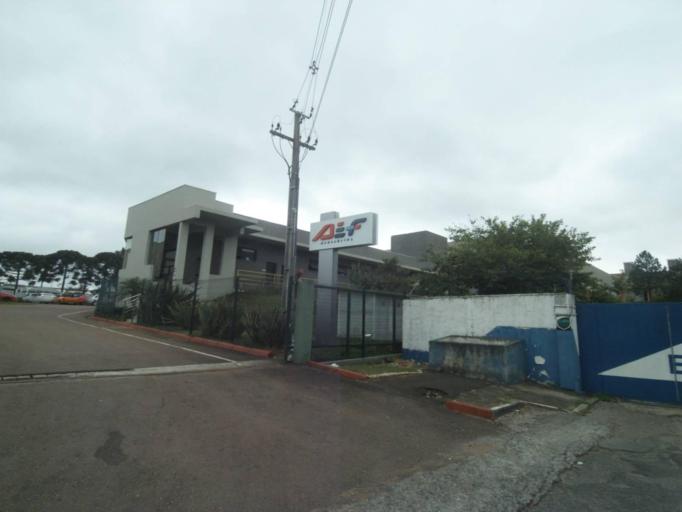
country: BR
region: Parana
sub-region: Sao Jose Dos Pinhais
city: Sao Jose dos Pinhais
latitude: -25.5292
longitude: -49.3175
